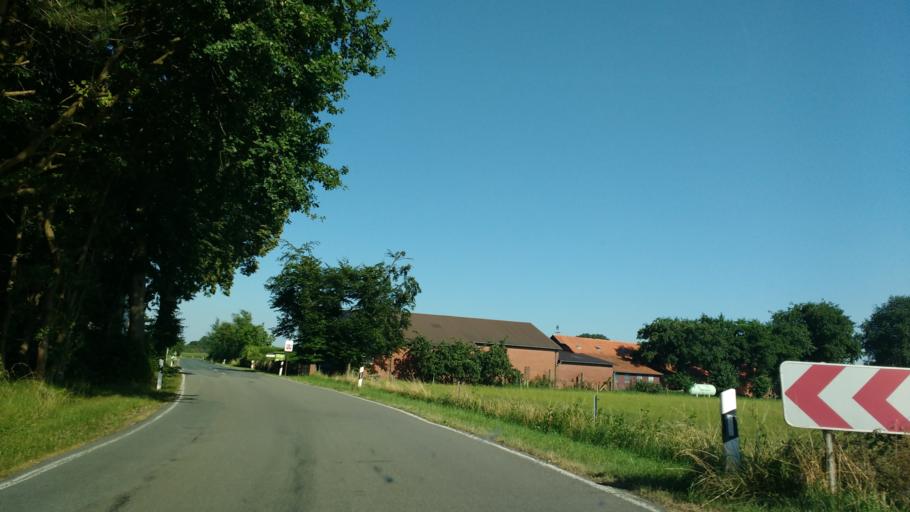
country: DE
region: North Rhine-Westphalia
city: Geseke
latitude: 51.7046
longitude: 8.4689
